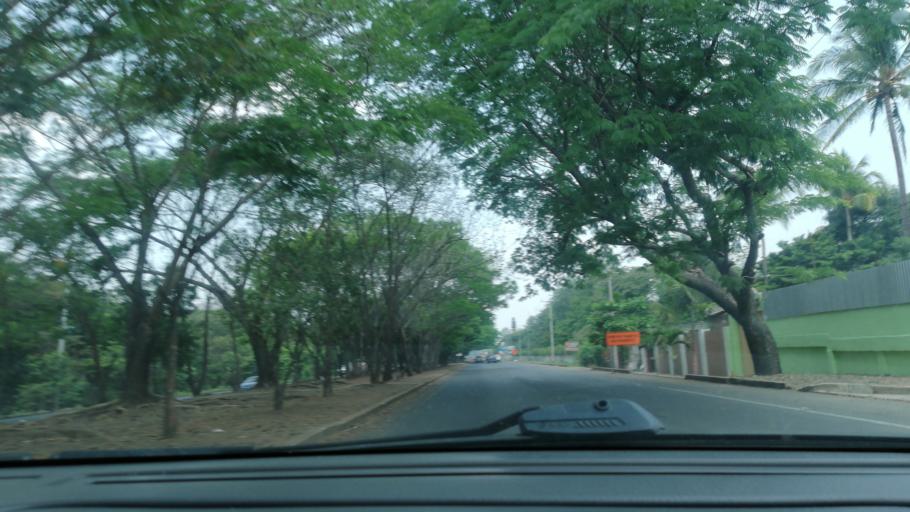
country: SV
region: Santa Ana
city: Chalchuapa
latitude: 13.9879
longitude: -89.6470
